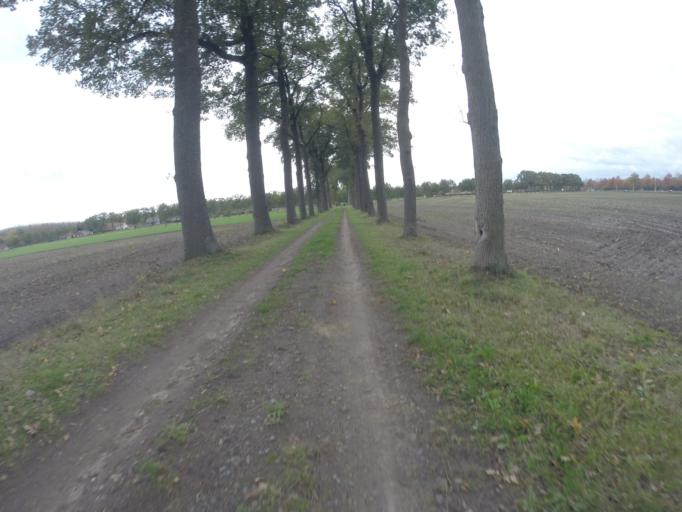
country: BE
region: Flanders
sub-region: Provincie Oost-Vlaanderen
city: Maldegem
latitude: 51.1687
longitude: 3.4465
